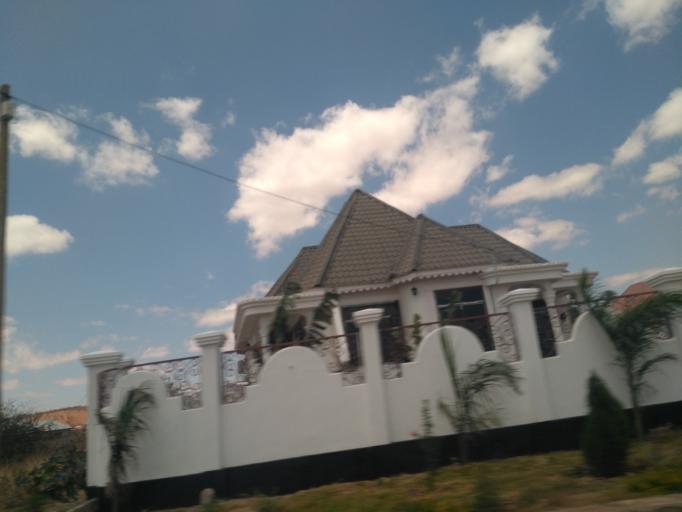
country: TZ
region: Dodoma
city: Kisasa
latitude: -6.1791
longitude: 35.7941
